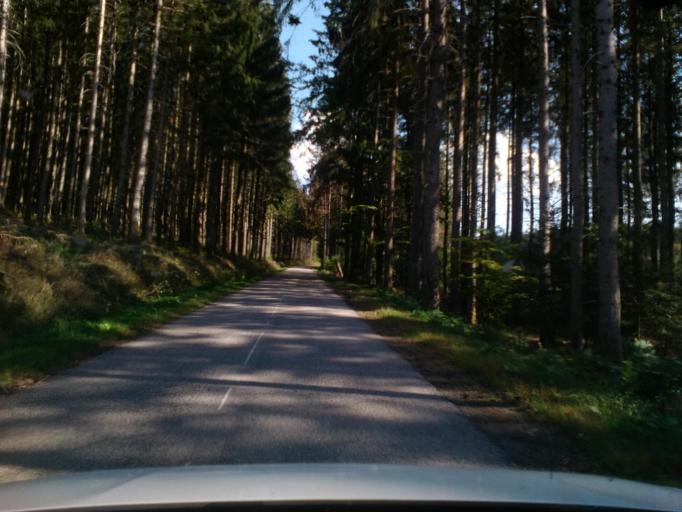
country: FR
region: Lorraine
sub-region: Departement des Vosges
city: Senones
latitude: 48.3389
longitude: 7.0462
